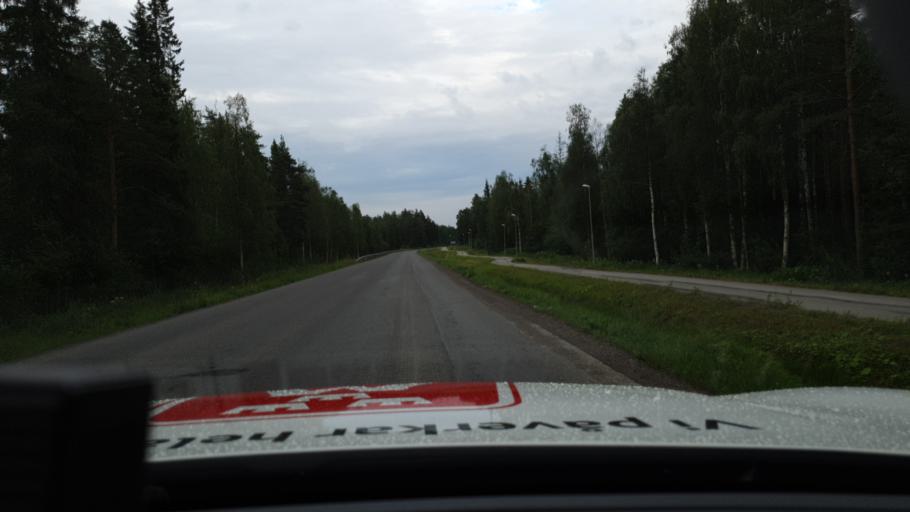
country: SE
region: Norrbotten
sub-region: Bodens Kommun
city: Boden
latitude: 65.8287
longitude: 21.6414
